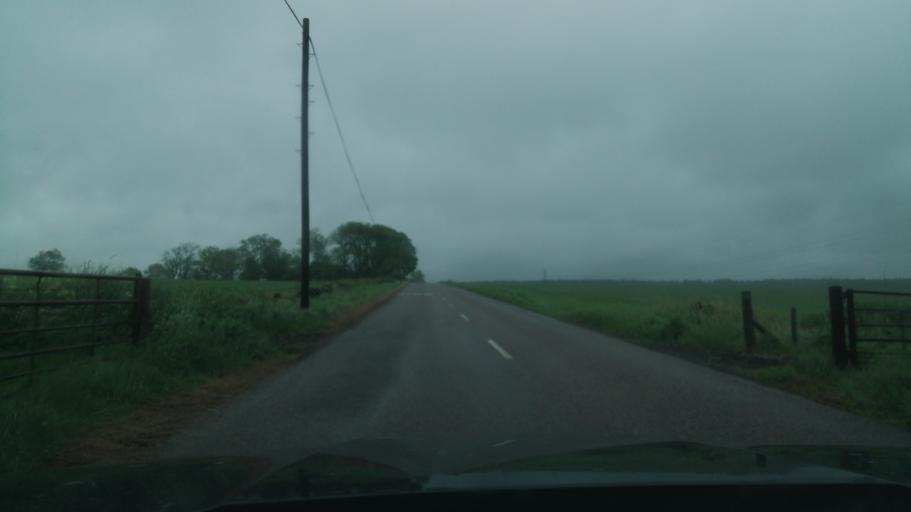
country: GB
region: Scotland
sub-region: Aberdeenshire
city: Huntly
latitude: 57.5474
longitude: -2.8182
